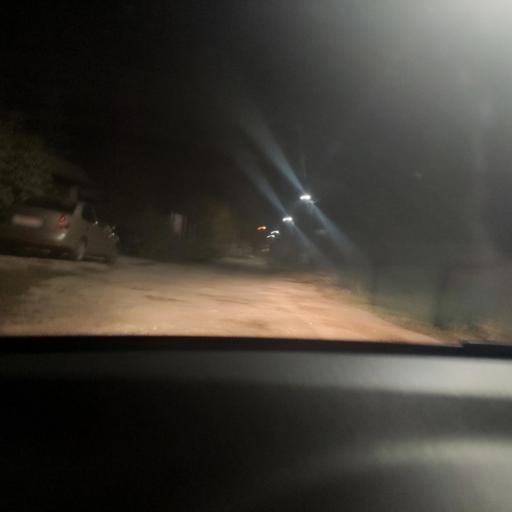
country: RU
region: Samara
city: Samara
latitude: 53.2248
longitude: 50.2180
